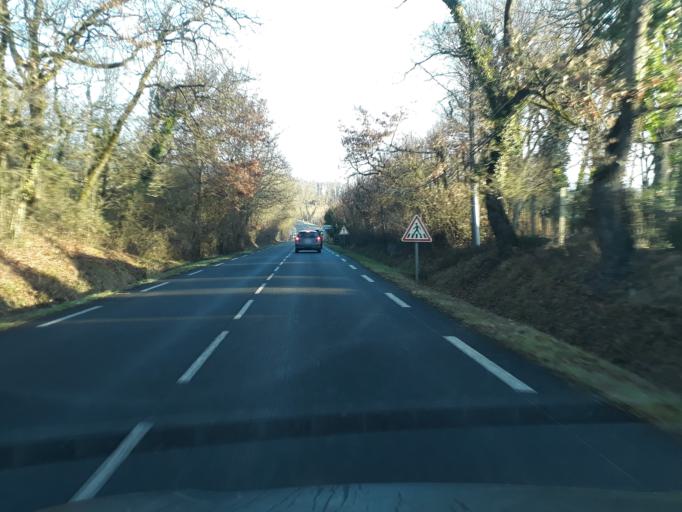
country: FR
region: Midi-Pyrenees
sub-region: Departement de la Haute-Garonne
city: Sainte-Foy-de-Peyrolieres
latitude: 43.4870
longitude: 1.1471
